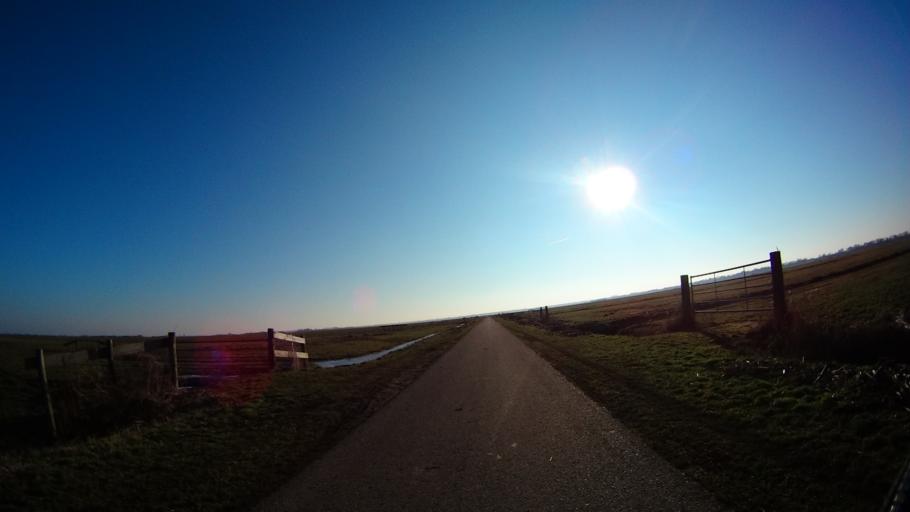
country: NL
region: North Holland
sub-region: Gemeente Blaricum
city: Blaricum
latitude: 52.2700
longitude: 5.2922
